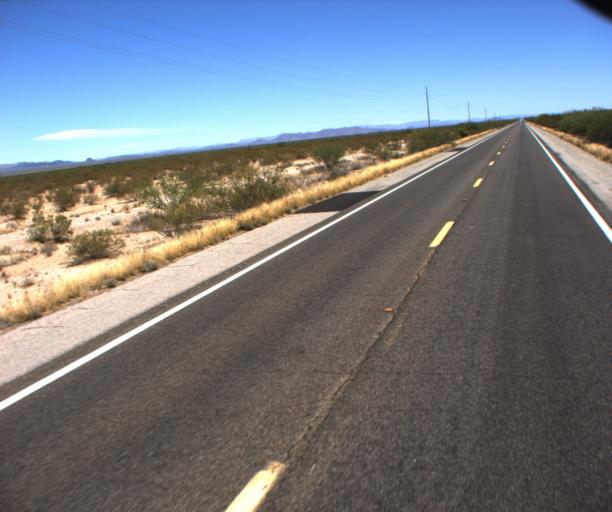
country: US
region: Arizona
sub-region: La Paz County
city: Salome
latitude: 33.8779
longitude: -113.3709
